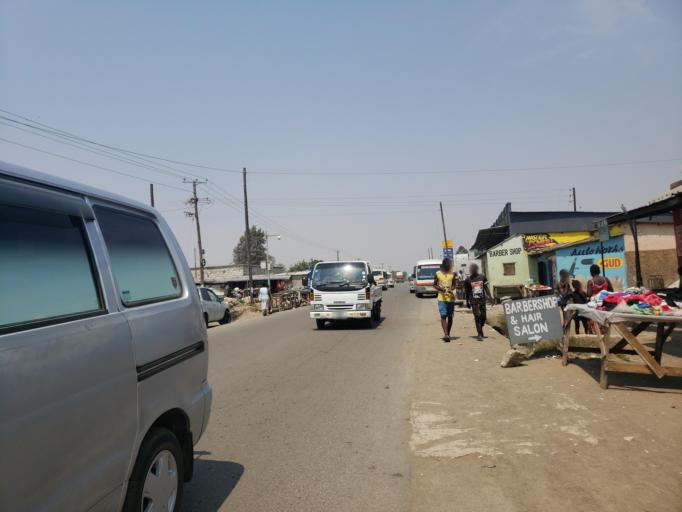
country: ZM
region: Lusaka
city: Lusaka
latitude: -15.4471
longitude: 28.2434
